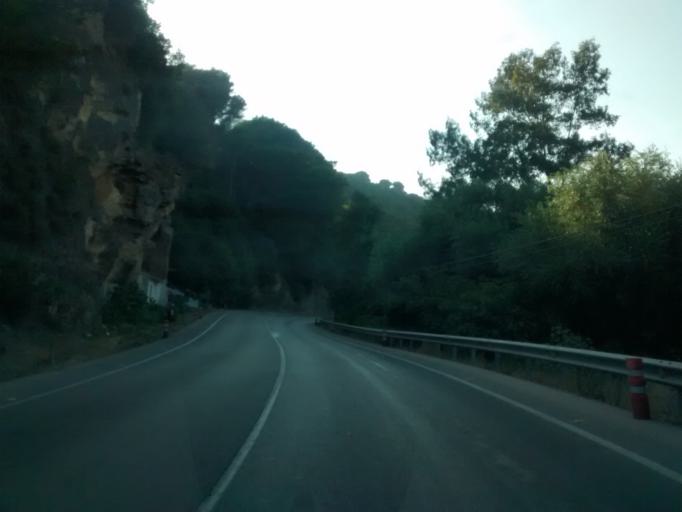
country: ES
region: Andalusia
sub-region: Provincia de Cadiz
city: Vejer de la Frontera
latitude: 36.2496
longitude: -5.9518
